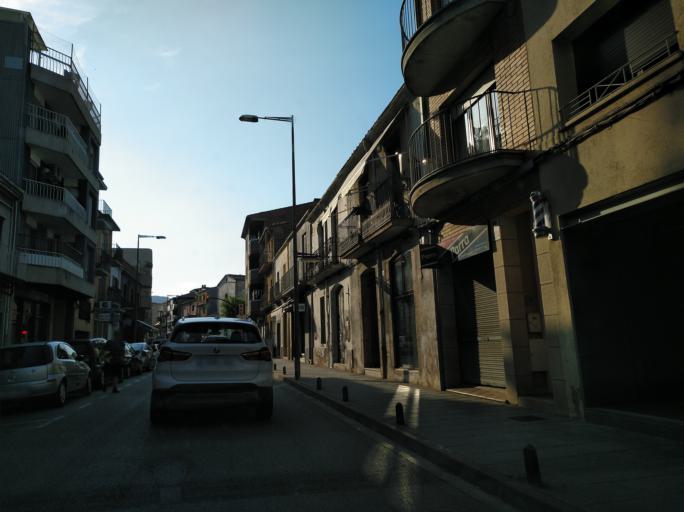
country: ES
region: Catalonia
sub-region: Provincia de Girona
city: Santa Coloma de Farners
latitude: 41.8604
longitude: 2.6686
